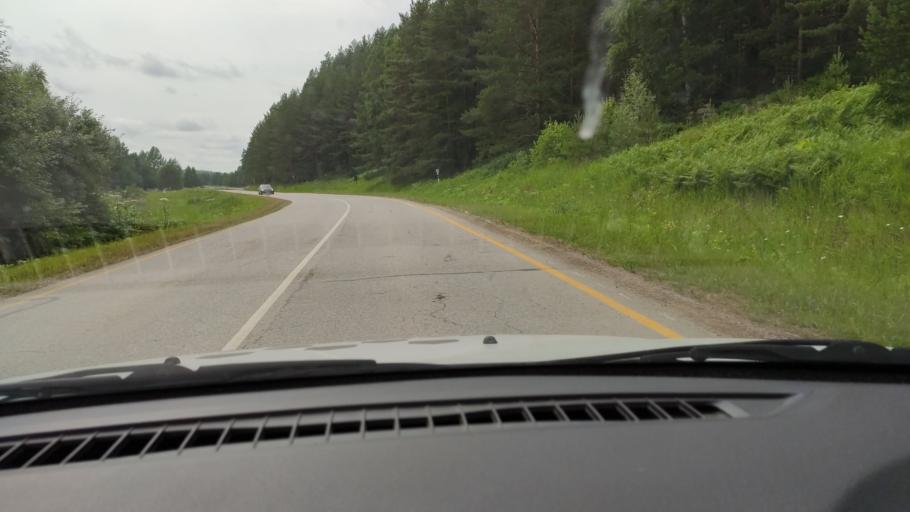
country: RU
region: Perm
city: Kukushtan
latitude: 57.4915
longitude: 56.6359
